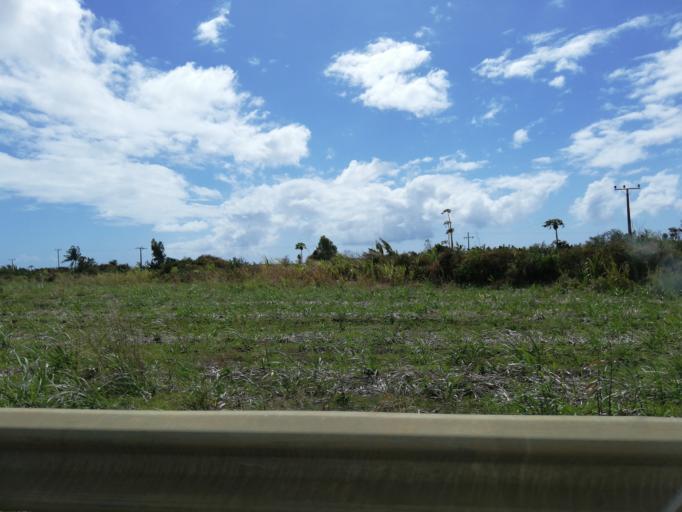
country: MU
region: Flacq
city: Mare La Chaux
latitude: -20.1897
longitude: 57.7363
